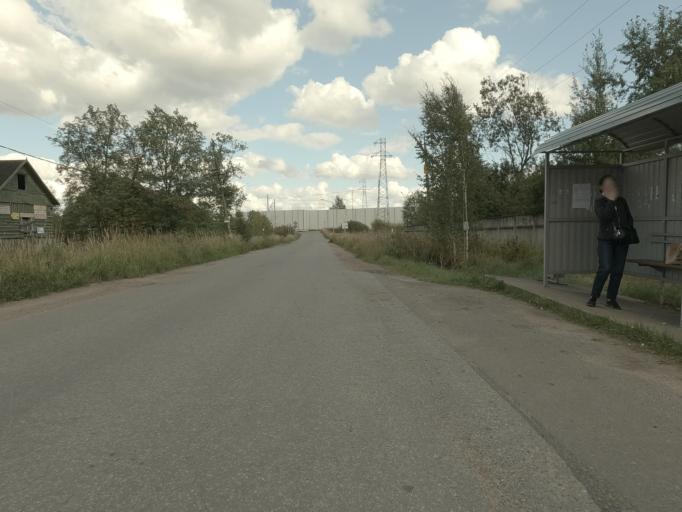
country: RU
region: Leningrad
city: Ul'yanovka
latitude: 59.6321
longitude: 30.7861
